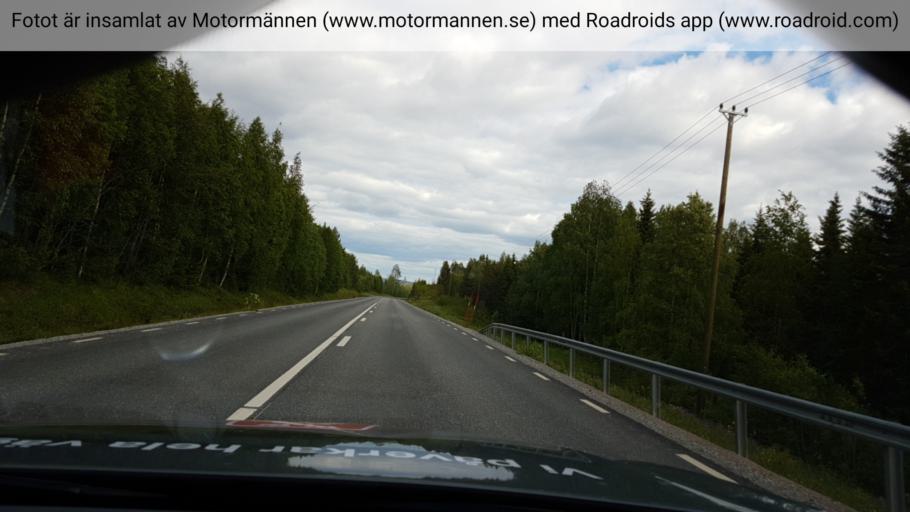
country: SE
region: Jaemtland
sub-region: Stroemsunds Kommun
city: Stroemsund
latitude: 64.1977
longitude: 15.6106
